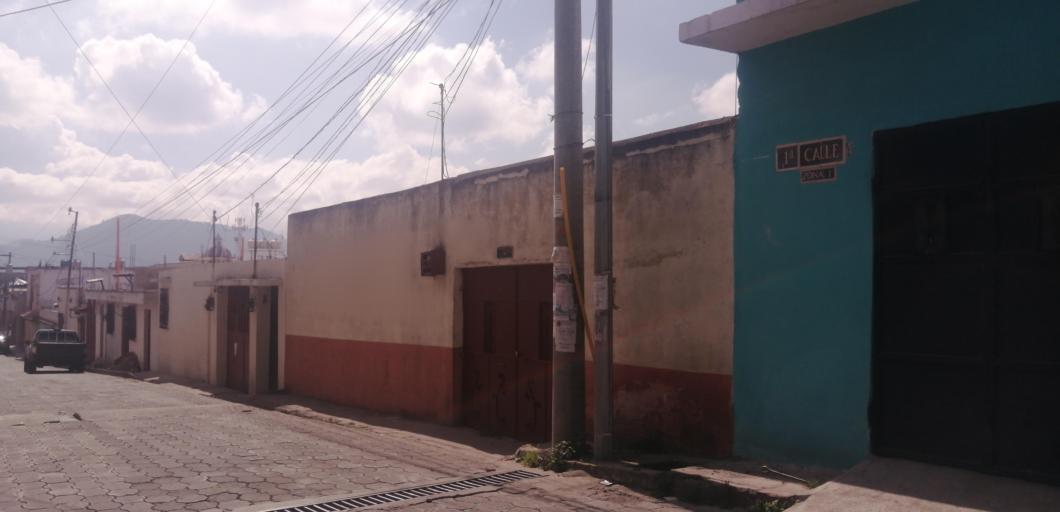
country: GT
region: Quetzaltenango
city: Quetzaltenango
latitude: 14.8427
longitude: -91.5321
